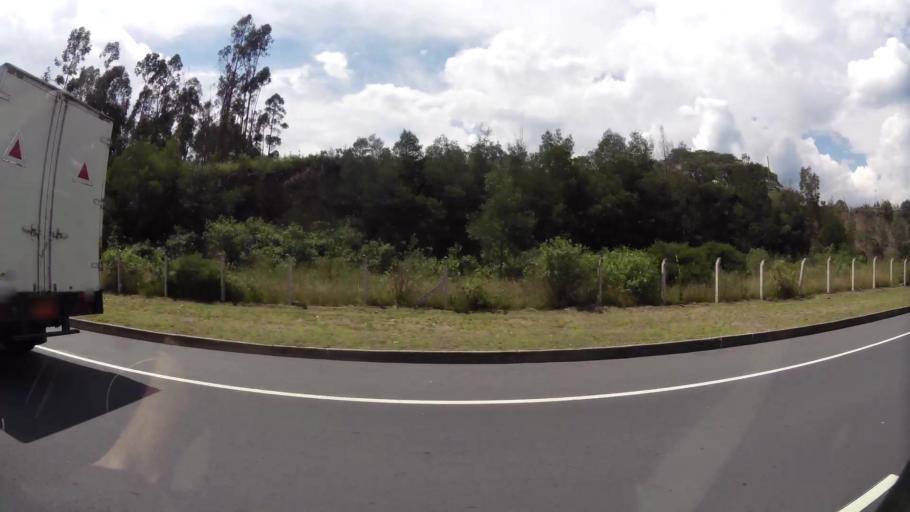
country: EC
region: Pichincha
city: Quito
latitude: -0.1782
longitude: -78.3417
